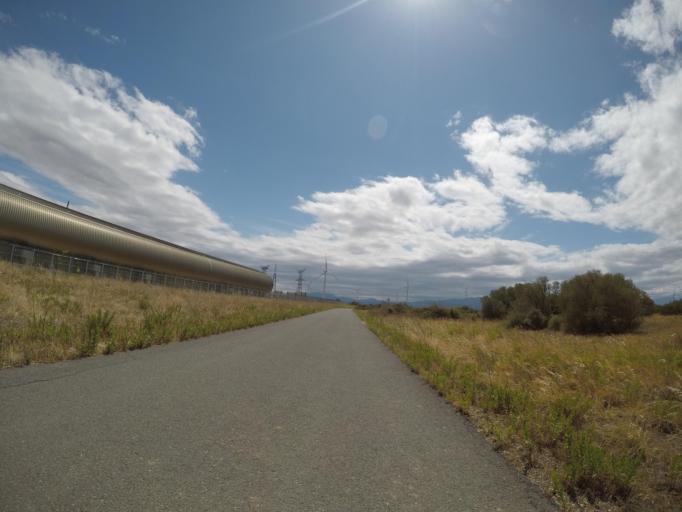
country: FR
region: Languedoc-Roussillon
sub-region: Departement des Pyrenees-Orientales
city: Baixas
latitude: 42.7321
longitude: 2.8002
